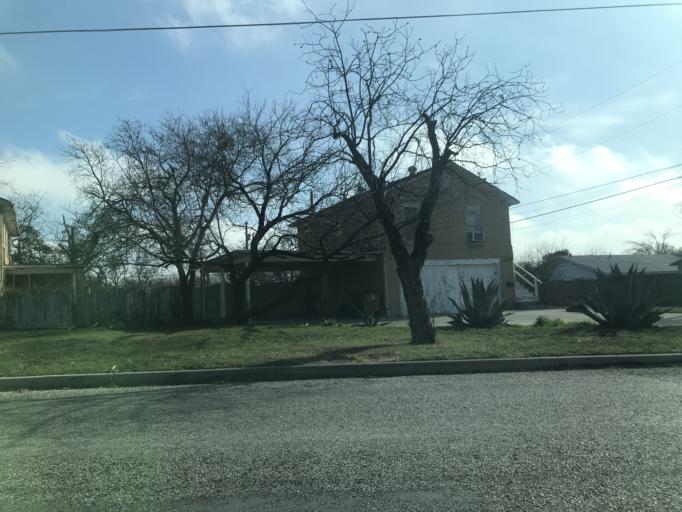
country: US
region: Texas
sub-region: Tom Green County
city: San Angelo
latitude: 31.4512
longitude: -100.4549
